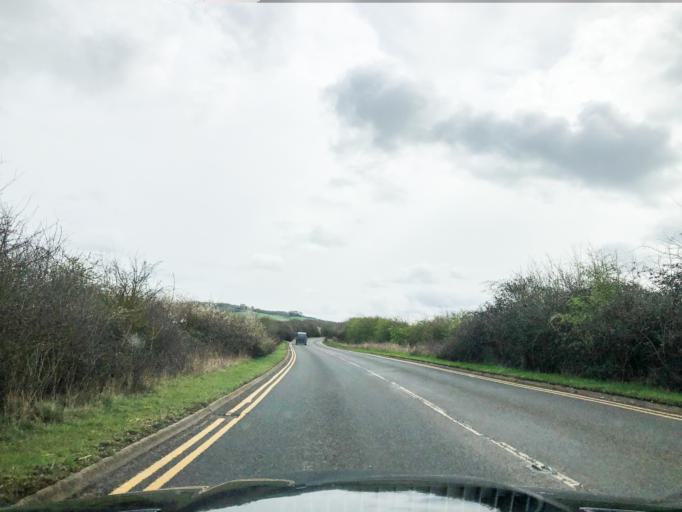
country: GB
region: England
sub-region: Warwickshire
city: Harbury
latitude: 52.1689
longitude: -1.4463
